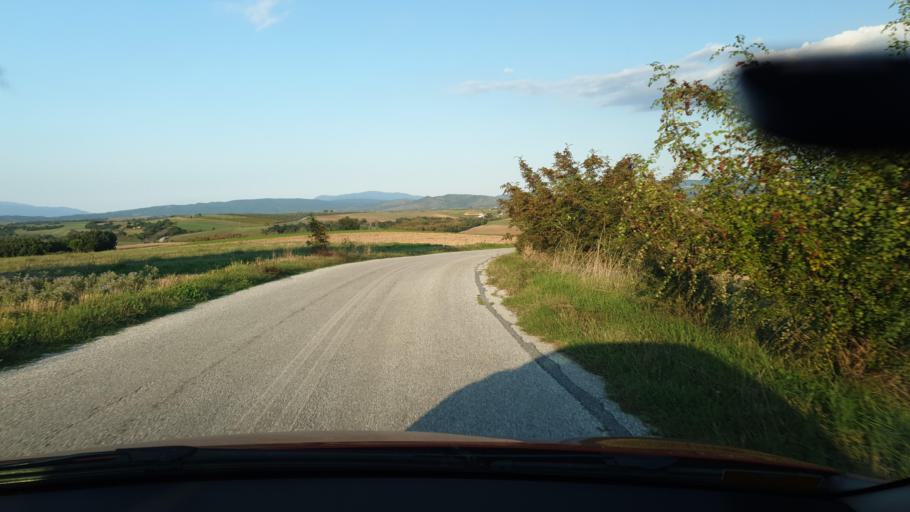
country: GR
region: Central Macedonia
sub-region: Nomos Thessalonikis
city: Nea Apollonia
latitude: 40.5490
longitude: 23.4211
